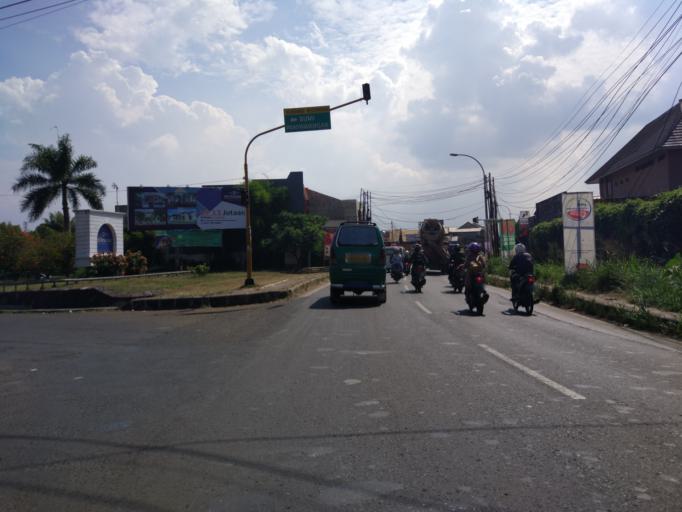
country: ID
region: West Java
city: Cileunyi
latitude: -6.9411
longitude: 107.7415
